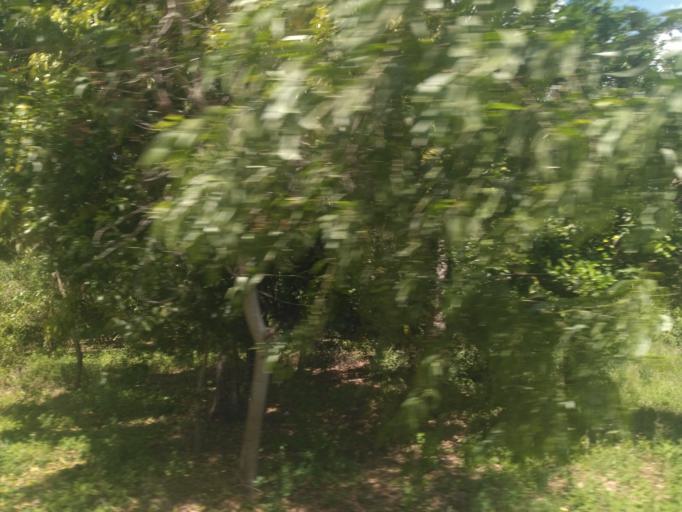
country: TZ
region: Zanzibar North
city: Gamba
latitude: -5.9313
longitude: 39.3410
